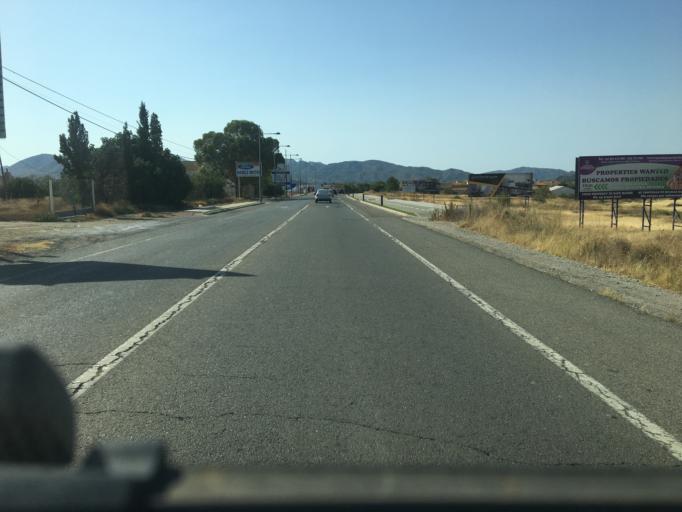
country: ES
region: Andalusia
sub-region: Provincia de Almeria
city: Huercal-Overa
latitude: 37.4065
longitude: -1.9574
